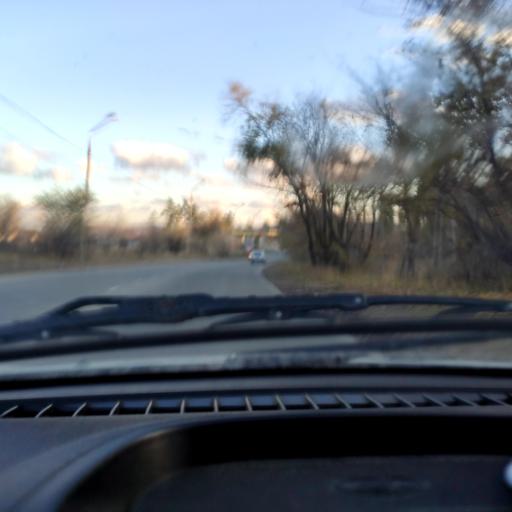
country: RU
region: Samara
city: Zhigulevsk
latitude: 53.4695
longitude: 49.5462
